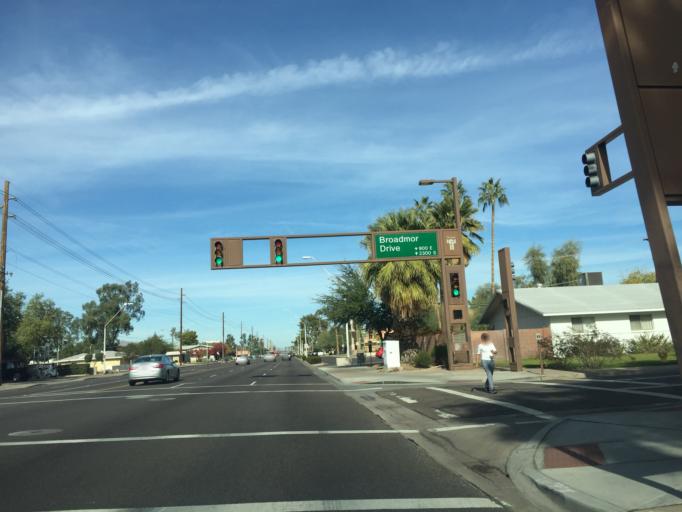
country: US
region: Arizona
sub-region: Maricopa County
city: Tempe
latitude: 33.4034
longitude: -111.9262
